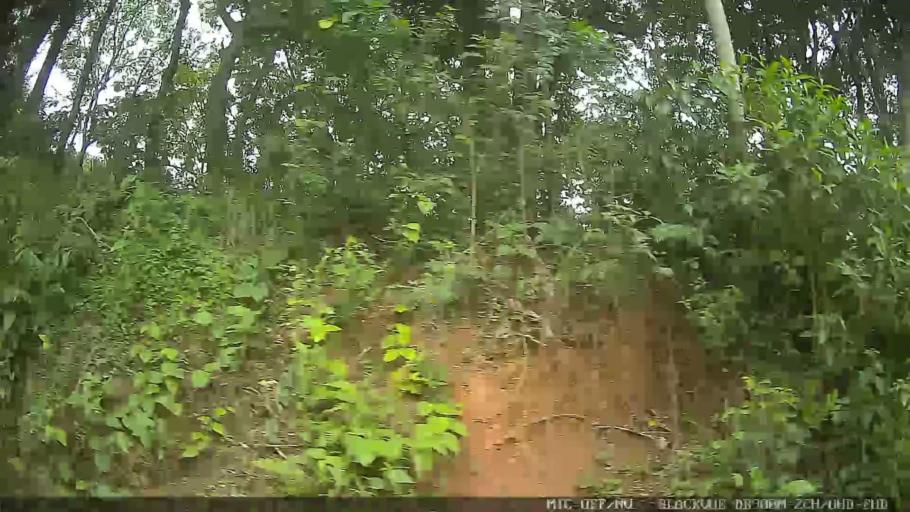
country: BR
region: Sao Paulo
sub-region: Santa Isabel
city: Santa Isabel
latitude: -23.3366
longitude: -46.2223
